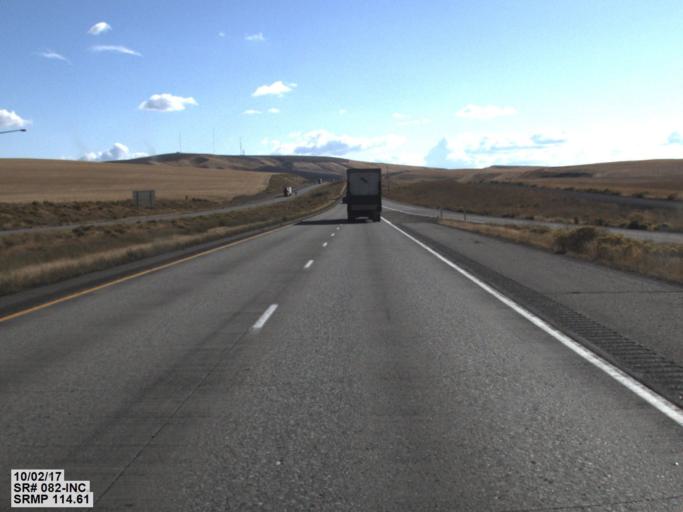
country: US
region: Washington
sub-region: Benton County
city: Highland
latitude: 46.1393
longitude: -119.2023
